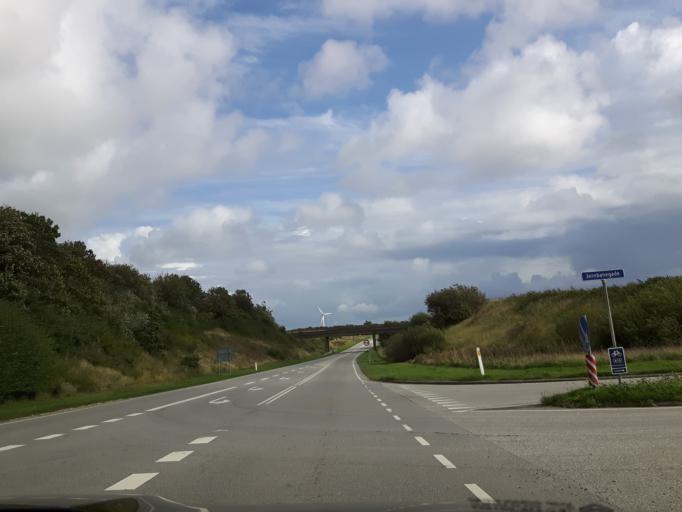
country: DK
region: North Denmark
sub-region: Thisted Kommune
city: Hurup
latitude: 56.7598
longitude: 8.4175
